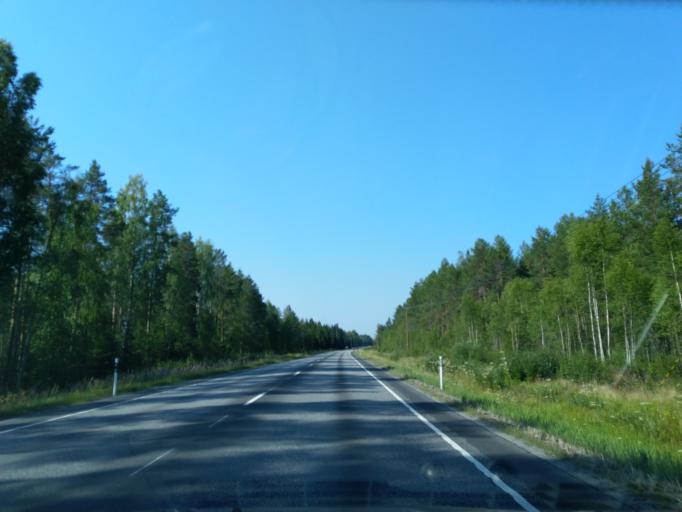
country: FI
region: Satakunta
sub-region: Pori
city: Pomarkku
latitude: 61.7119
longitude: 22.0375
